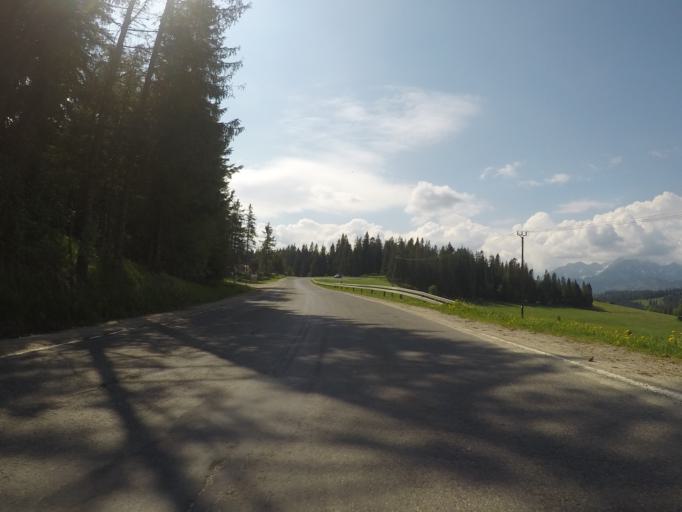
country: PL
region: Lesser Poland Voivodeship
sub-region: Powiat tatrzanski
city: Bukowina Tatrzanska
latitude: 49.3214
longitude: 20.1058
